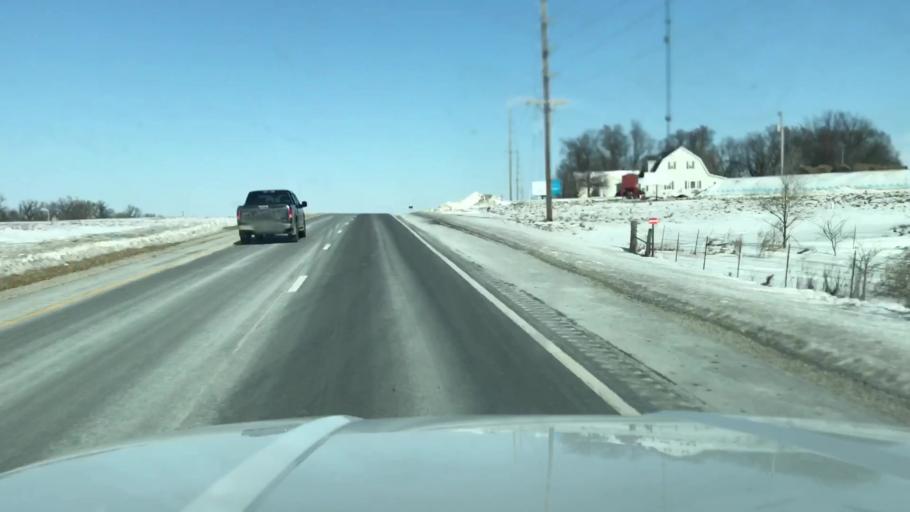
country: US
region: Missouri
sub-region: Nodaway County
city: Maryville
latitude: 40.1785
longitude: -94.8687
